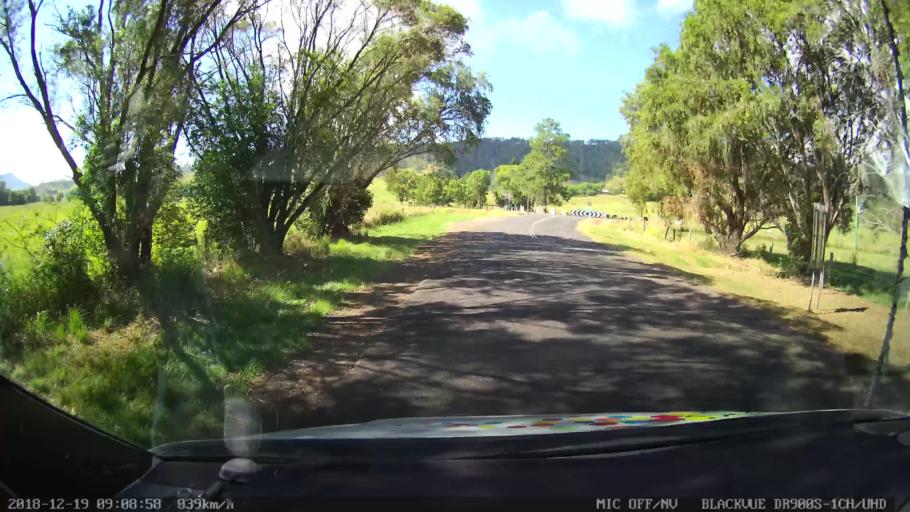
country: AU
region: New South Wales
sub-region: Kyogle
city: Kyogle
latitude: -28.4858
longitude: 152.9304
